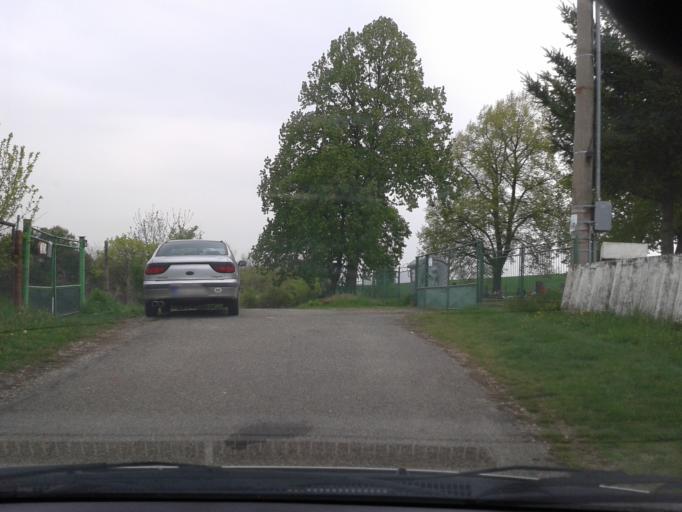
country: SK
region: Banskobystricky
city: Dudince
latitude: 48.1887
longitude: 18.8551
